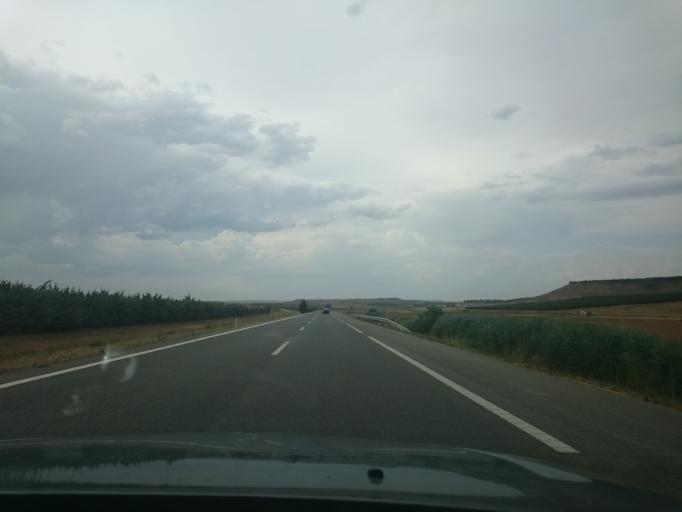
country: ES
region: Navarre
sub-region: Provincia de Navarra
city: Fontellas
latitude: 41.9993
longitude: -1.5824
